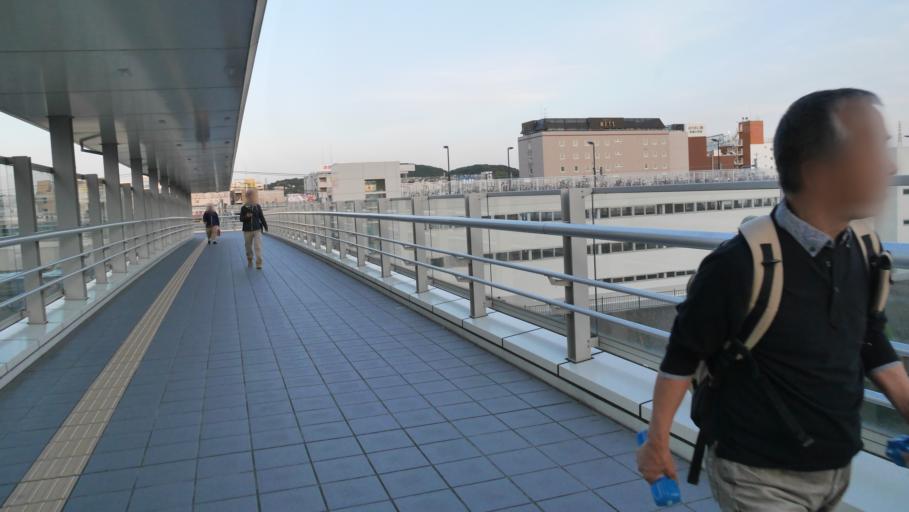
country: JP
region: Kanagawa
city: Kamakura
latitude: 35.3524
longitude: 139.5294
